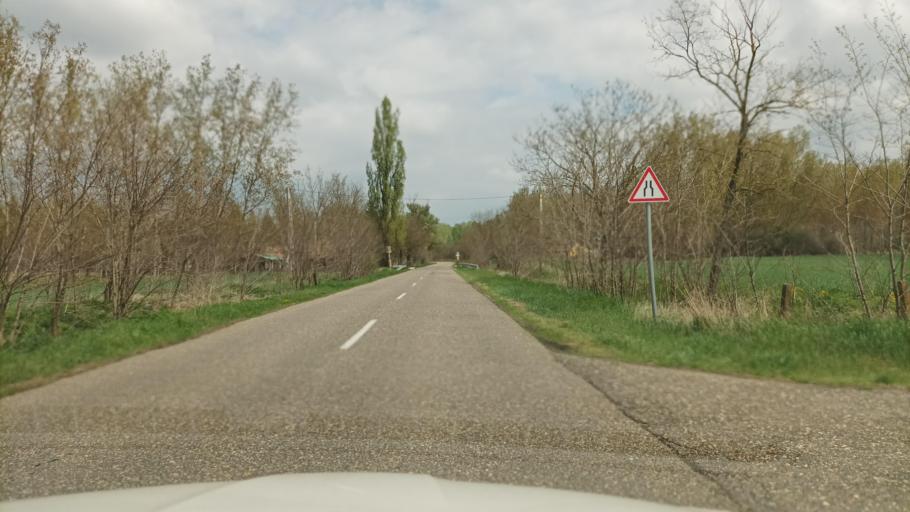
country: HU
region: Pest
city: Nagykoros
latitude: 47.0606
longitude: 19.8587
